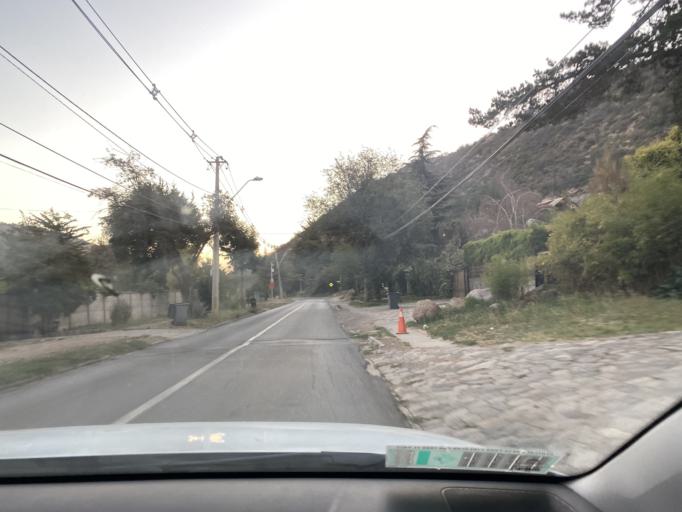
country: CL
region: Santiago Metropolitan
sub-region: Provincia de Santiago
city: Villa Presidente Frei, Nunoa, Santiago, Chile
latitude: -33.3585
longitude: -70.4842
